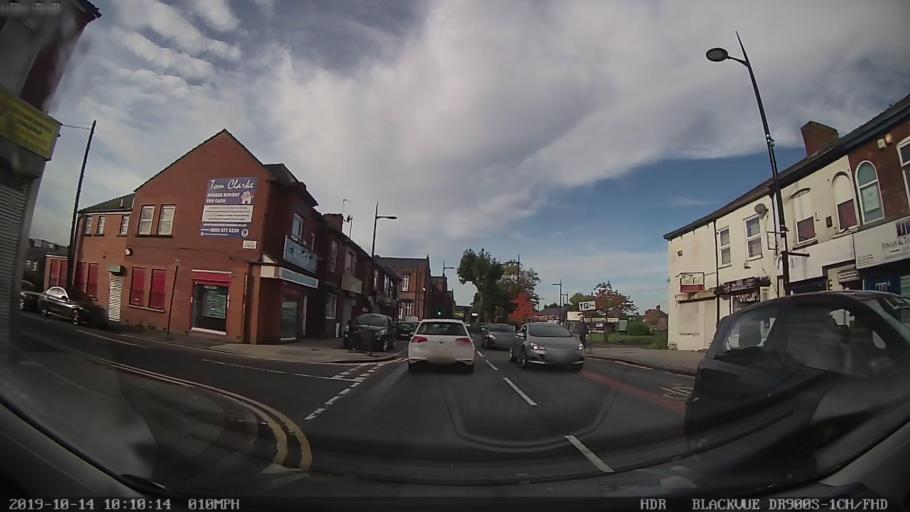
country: GB
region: England
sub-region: Manchester
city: Blackley
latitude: 53.5138
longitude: -2.2010
